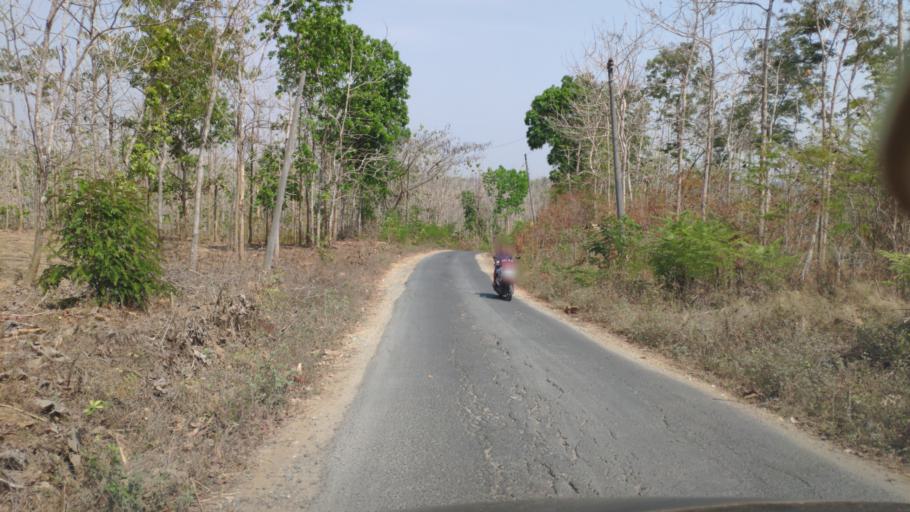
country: ID
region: Central Java
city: Gaplokan
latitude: -6.9079
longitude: 111.2707
